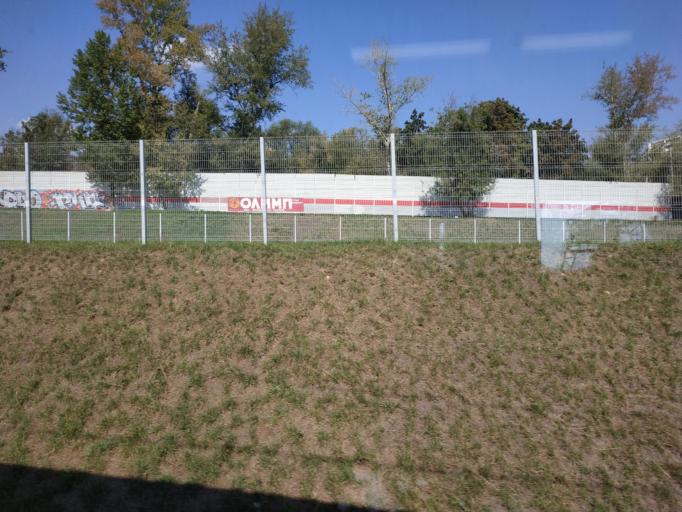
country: RU
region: Moscow
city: Novyye Cheremushki
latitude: 55.6891
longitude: 37.6112
